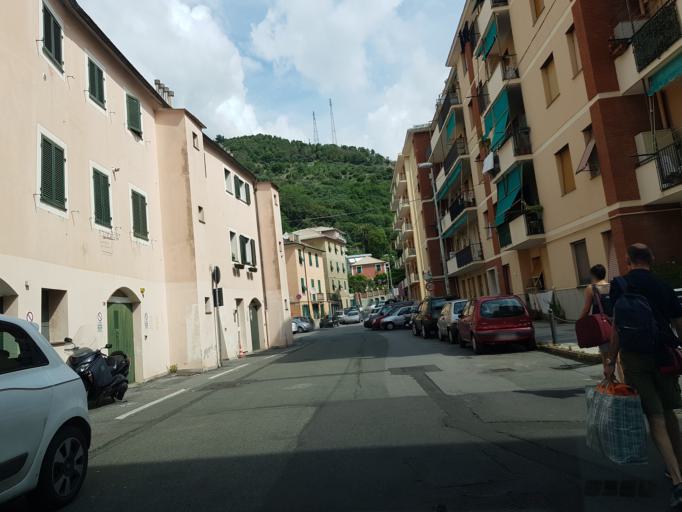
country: IT
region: Liguria
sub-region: Provincia di Genova
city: San Teodoro
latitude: 44.4330
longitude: 8.8516
